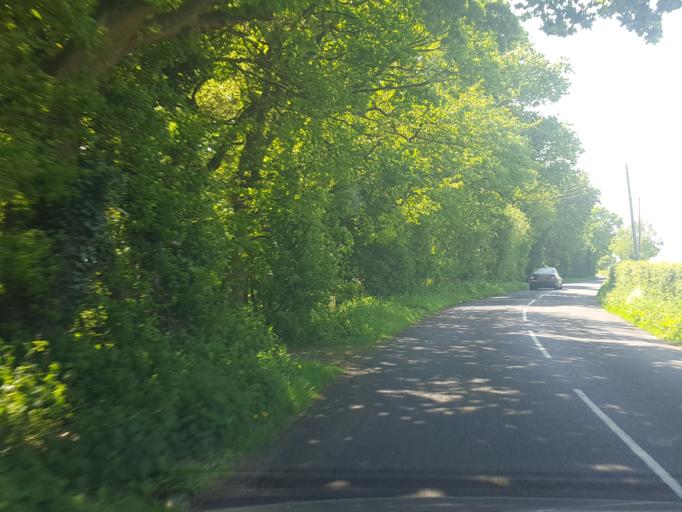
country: GB
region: England
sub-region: Essex
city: Great Bentley
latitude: 51.8587
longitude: 1.0910
